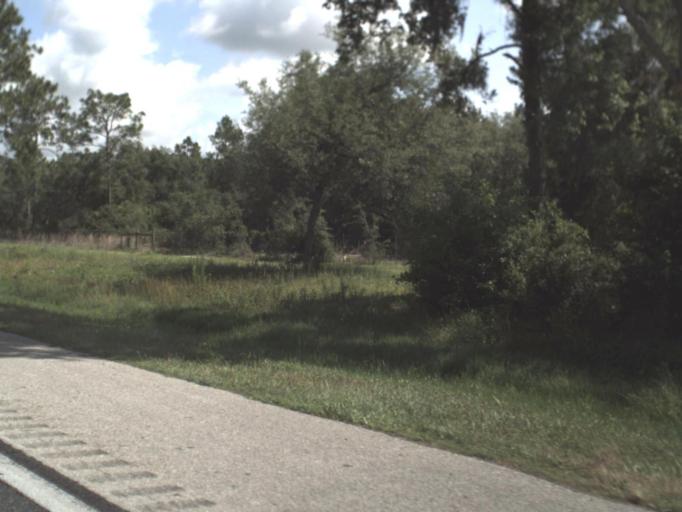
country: US
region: Florida
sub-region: Alachua County
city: Gainesville
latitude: 29.5144
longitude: -82.3034
